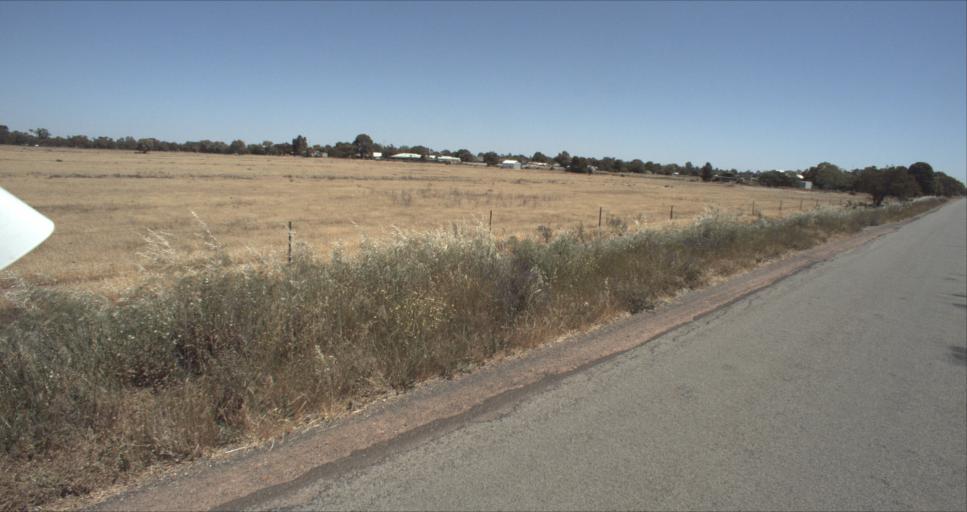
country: AU
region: New South Wales
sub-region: Leeton
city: Leeton
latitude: -34.5446
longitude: 146.4239
